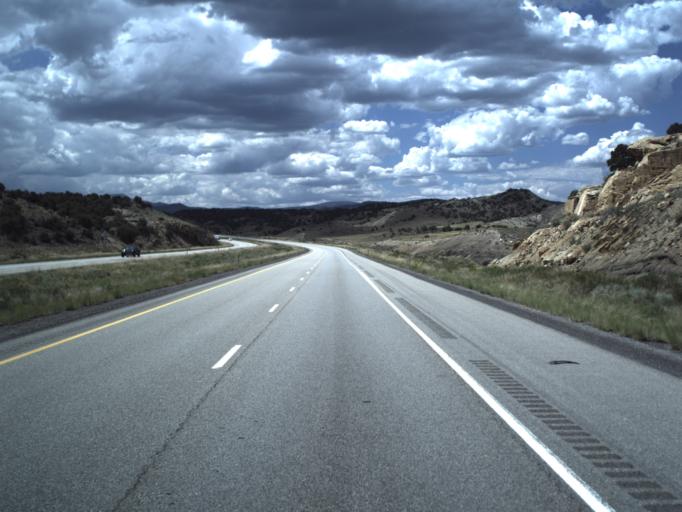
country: US
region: Utah
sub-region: Emery County
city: Ferron
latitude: 38.7990
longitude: -111.2787
